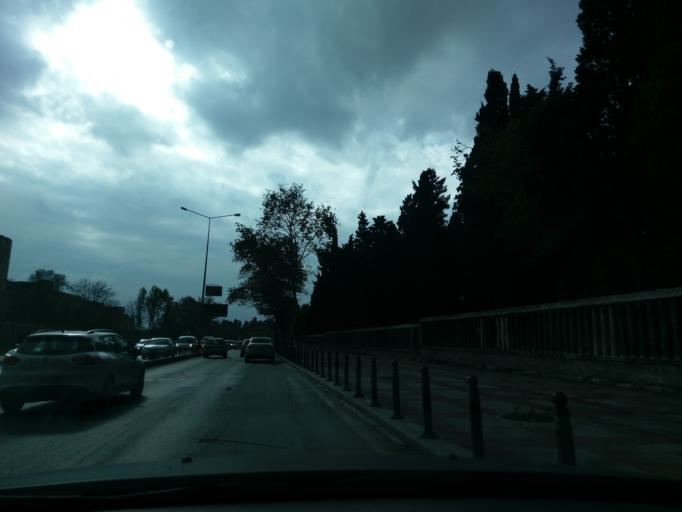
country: TR
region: Istanbul
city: Zeytinburnu
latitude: 41.0154
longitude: 28.9215
